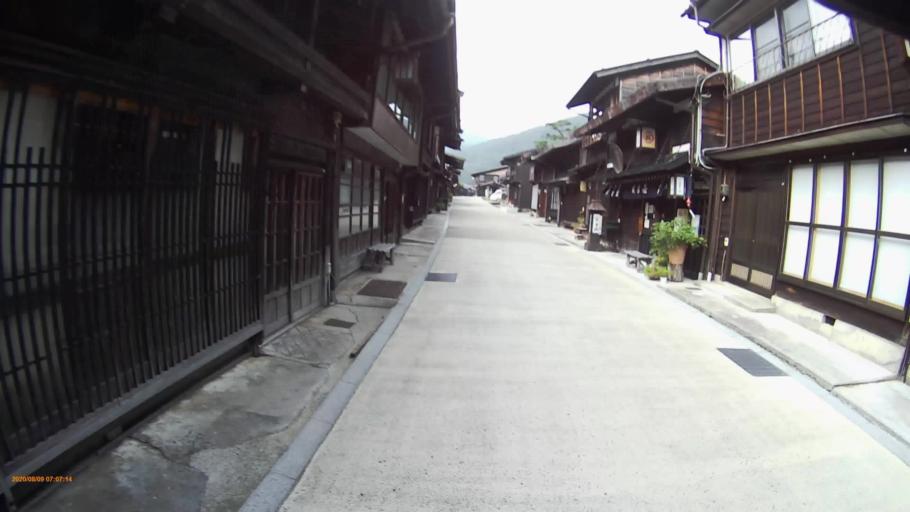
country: JP
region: Nagano
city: Tatsuno
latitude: 35.9667
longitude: 137.8124
